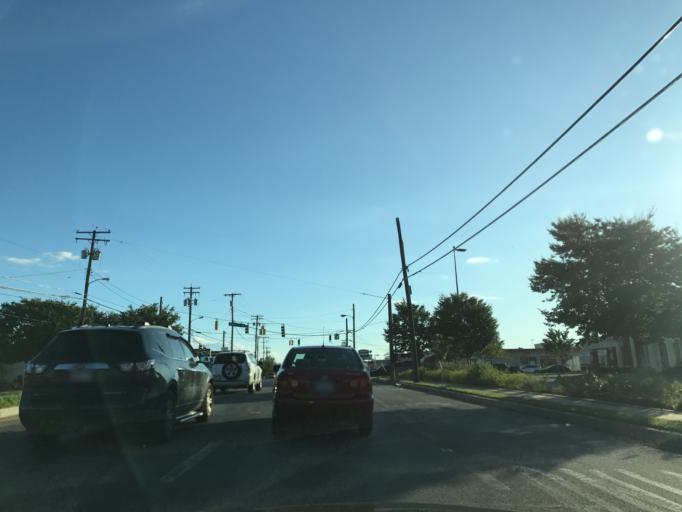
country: US
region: Maryland
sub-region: Prince George's County
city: Laurel
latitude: 39.0953
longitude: -76.8531
